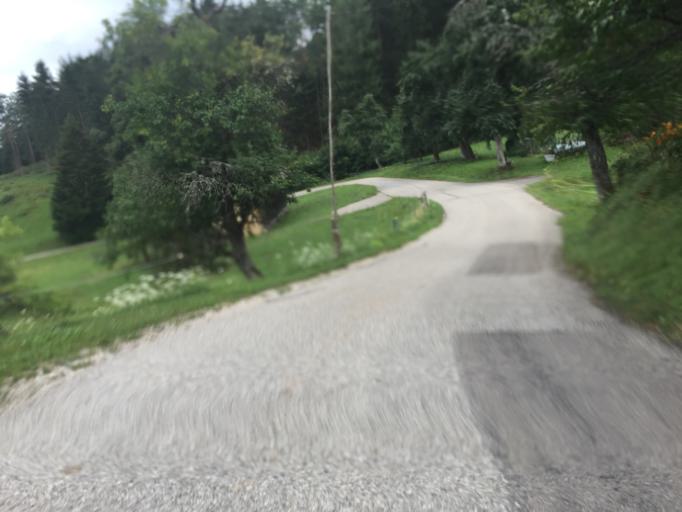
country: AT
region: Carinthia
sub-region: Politischer Bezirk Volkermarkt
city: Feistritz ob Bleiburg
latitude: 46.5409
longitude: 14.7806
